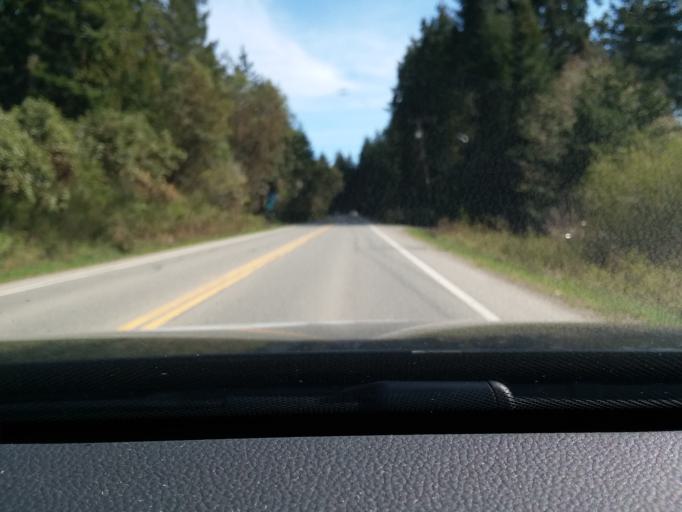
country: CA
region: British Columbia
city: North Saanich
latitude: 48.8550
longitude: -123.4740
